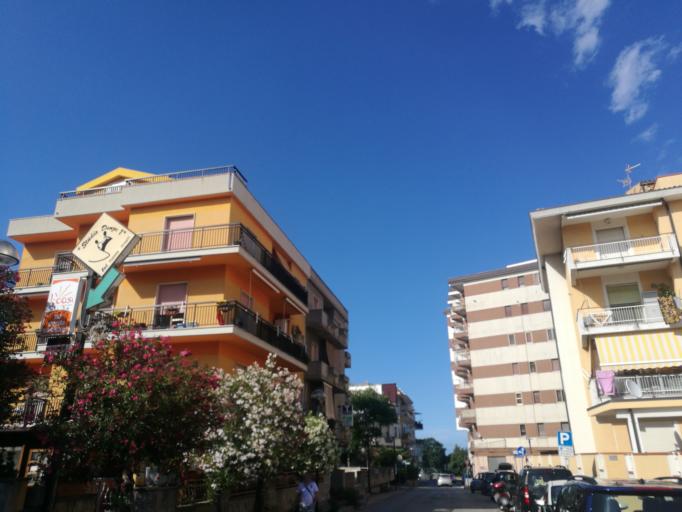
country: IT
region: Molise
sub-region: Provincia di Campobasso
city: Termoli
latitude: 41.9929
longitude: 14.9966
